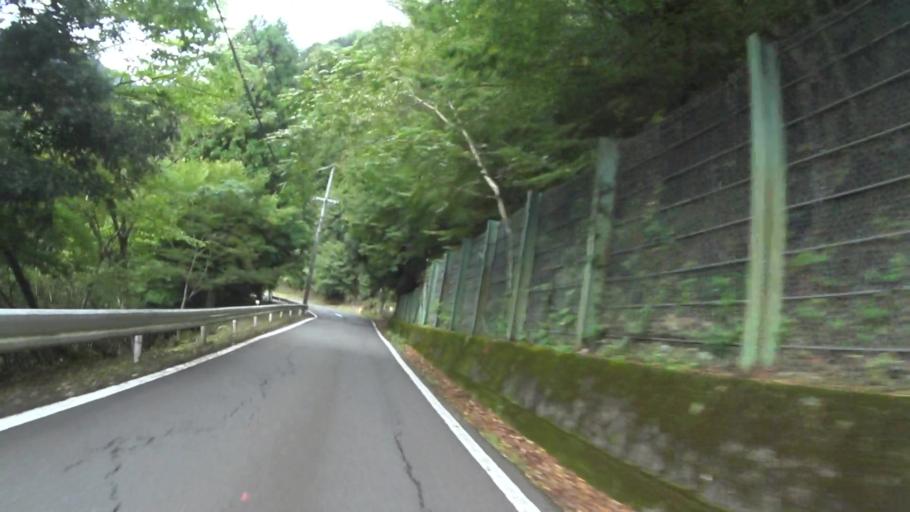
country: JP
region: Fukui
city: Obama
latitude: 35.3125
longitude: 135.6915
